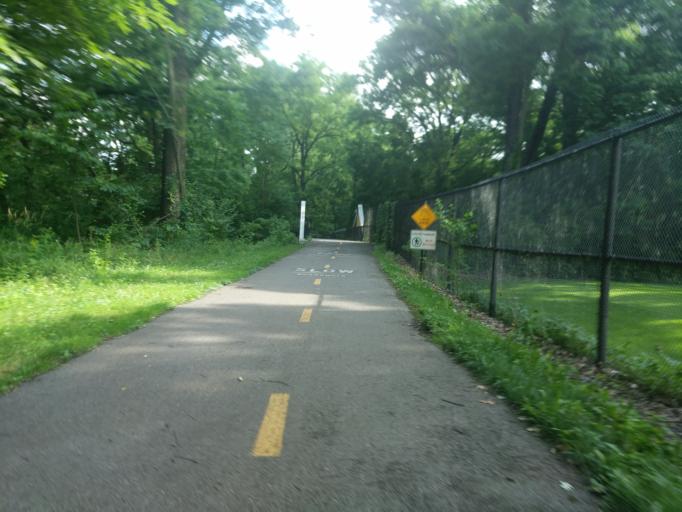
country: US
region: Ohio
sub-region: Franklin County
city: Minerva Park
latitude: 40.0447
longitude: -82.9333
